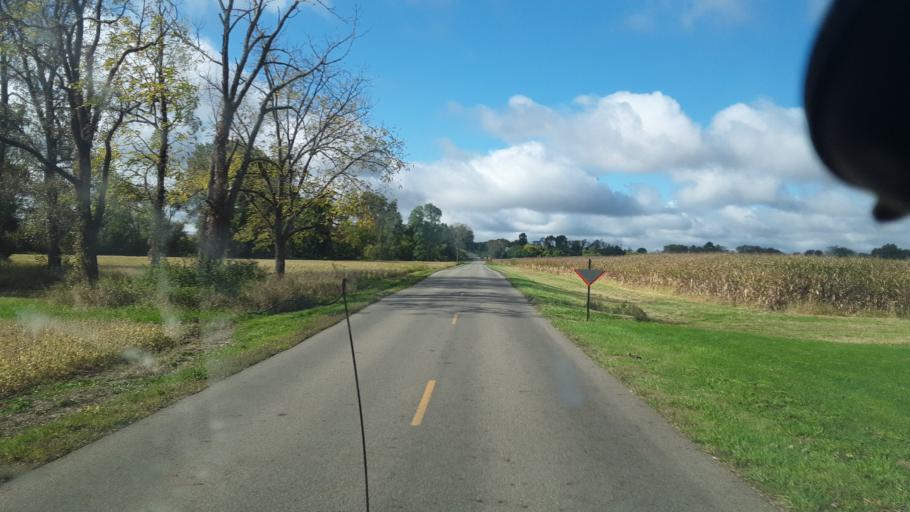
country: US
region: Ohio
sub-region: Knox County
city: Centerburg
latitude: 40.2761
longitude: -82.6518
